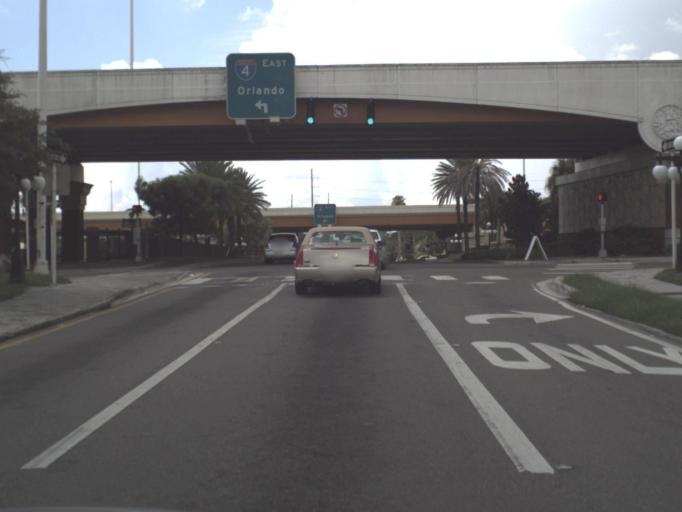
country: US
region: Florida
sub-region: Hillsborough County
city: Tampa
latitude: 27.9660
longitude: -82.4355
